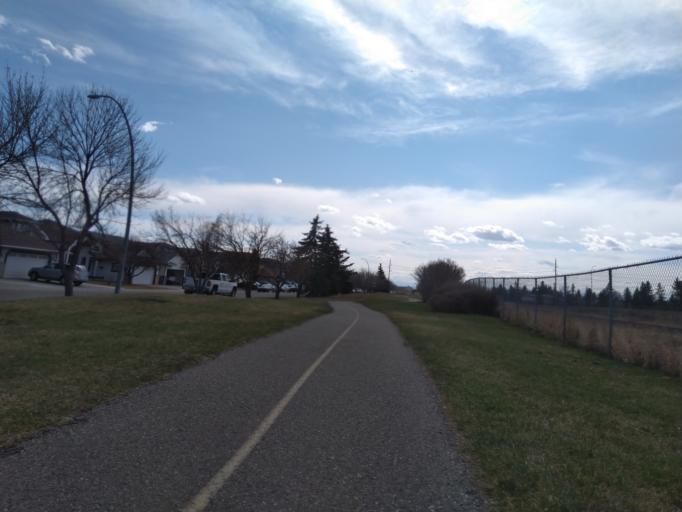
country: CA
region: Alberta
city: Chestermere
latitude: 51.0487
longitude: -113.9325
